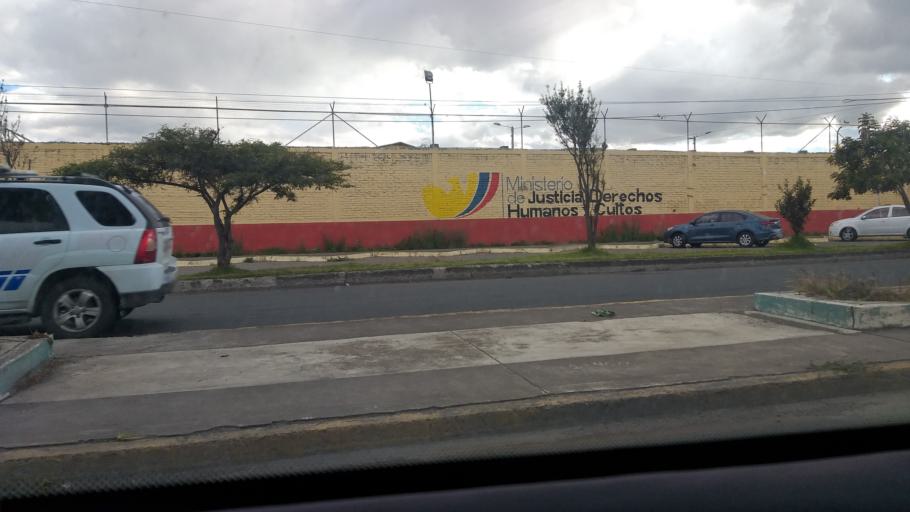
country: EC
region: Chimborazo
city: Riobamba
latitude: -1.6911
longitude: -78.6307
